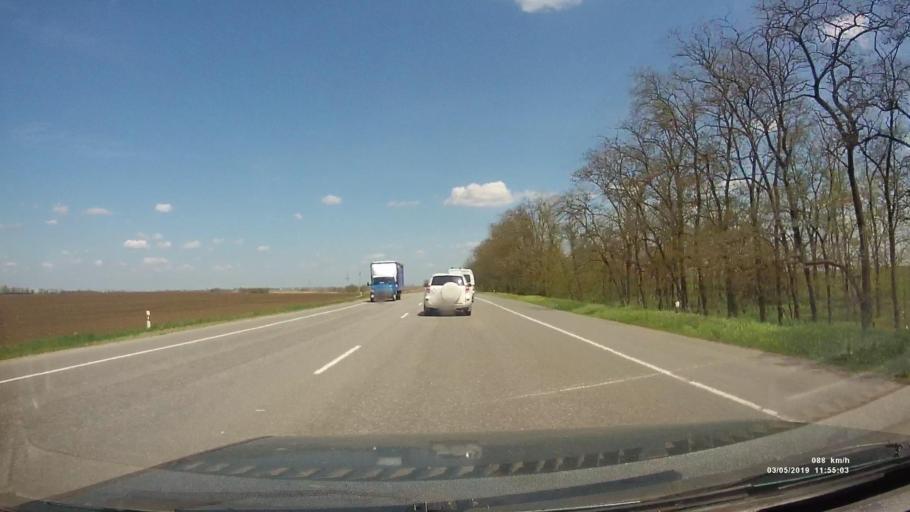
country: RU
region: Rostov
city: Bagayevskaya
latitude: 47.1761
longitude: 40.2876
